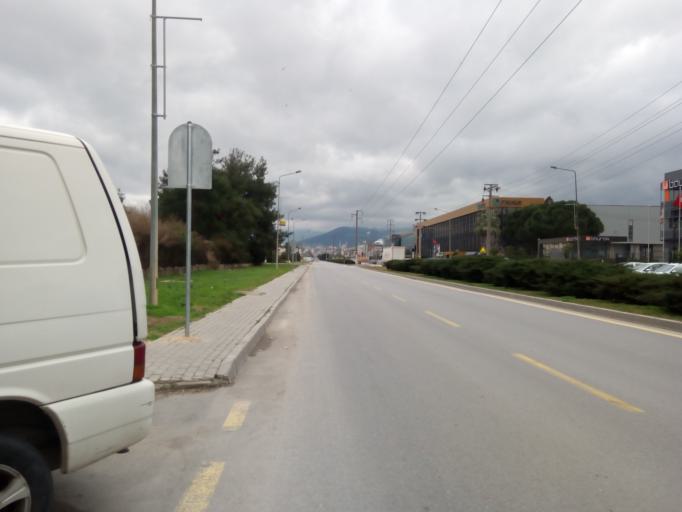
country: TR
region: Bursa
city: Niluefer
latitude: 40.2463
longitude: 28.9575
